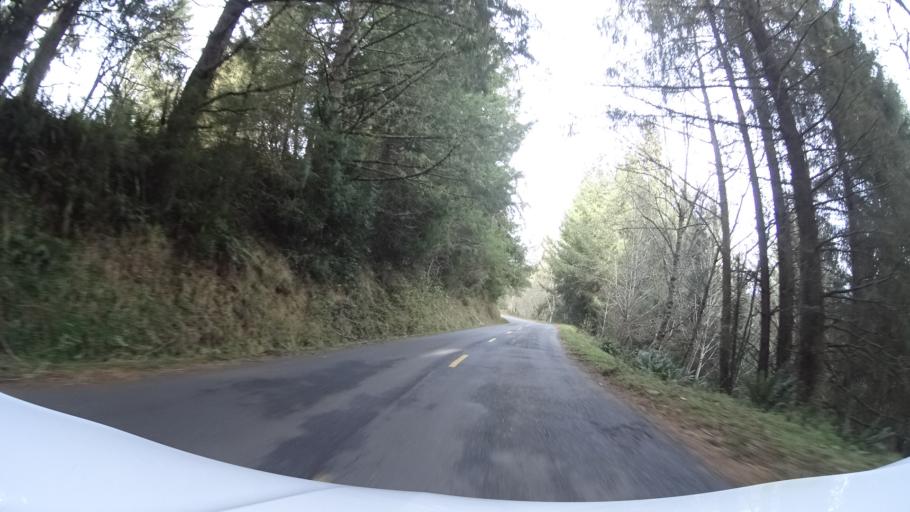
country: US
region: California
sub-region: Humboldt County
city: Ferndale
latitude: 40.5483
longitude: -124.2754
